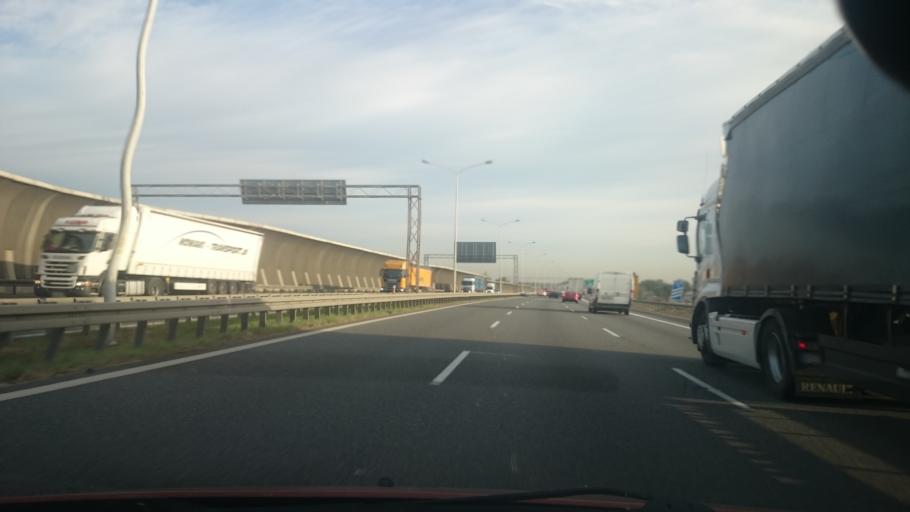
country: PL
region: Lower Silesian Voivodeship
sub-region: Powiat wroclawski
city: Smolec
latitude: 51.1244
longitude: 16.9334
